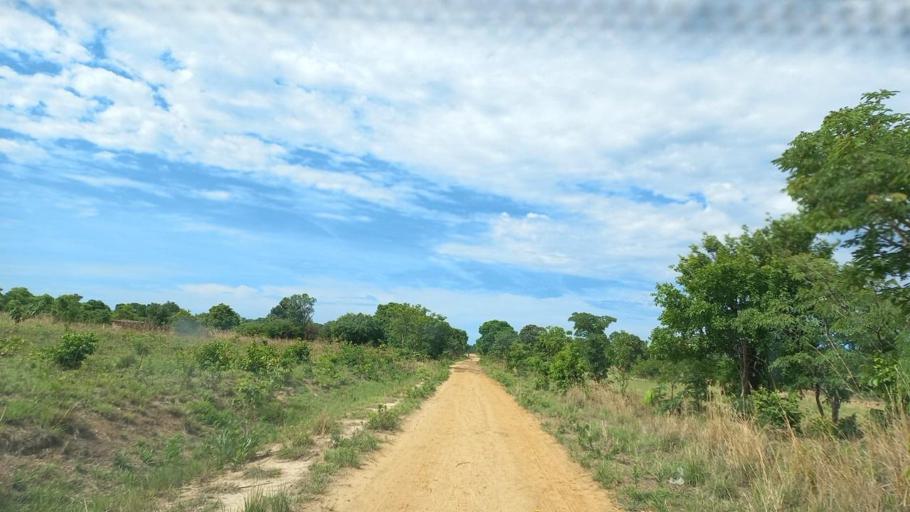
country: ZM
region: North-Western
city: Kabompo
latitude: -13.5190
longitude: 24.3863
